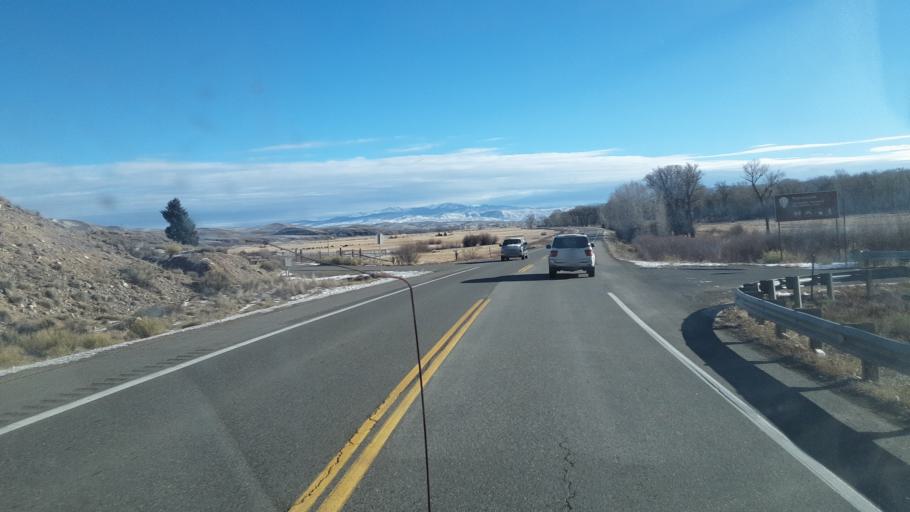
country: US
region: Colorado
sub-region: Gunnison County
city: Gunnison
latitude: 38.5169
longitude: -107.0182
